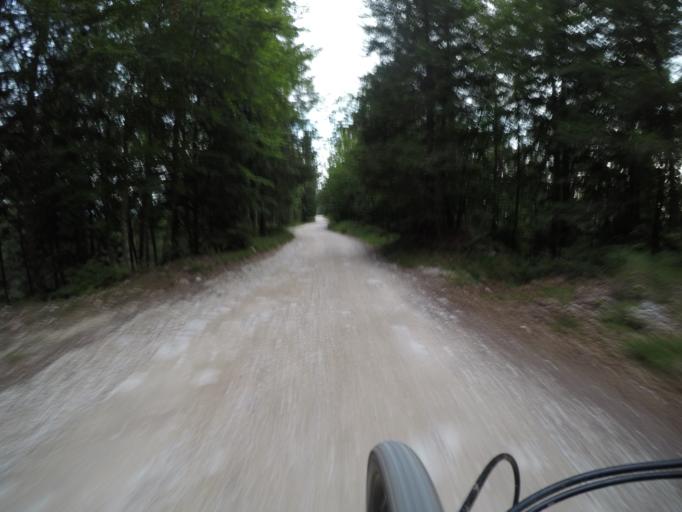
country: IT
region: Veneto
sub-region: Provincia di Vicenza
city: Gallio
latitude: 45.9045
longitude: 11.5252
